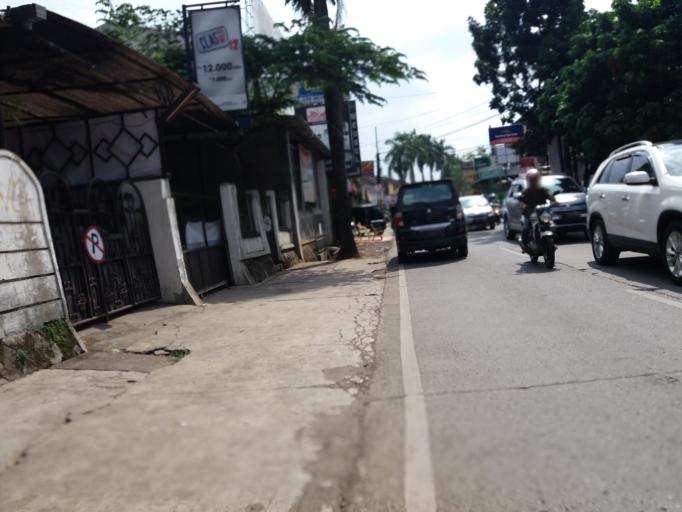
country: ID
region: West Java
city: Bandung
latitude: -6.9164
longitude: 107.6544
